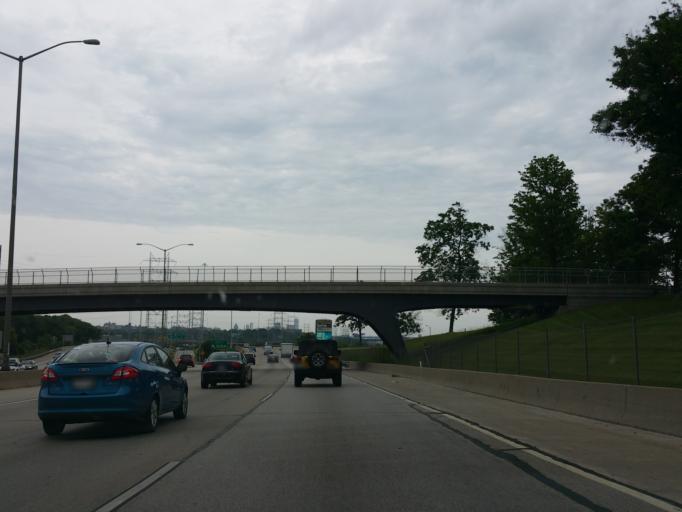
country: US
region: Wisconsin
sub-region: Milwaukee County
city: West Milwaukee
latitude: 43.0303
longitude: -87.9816
